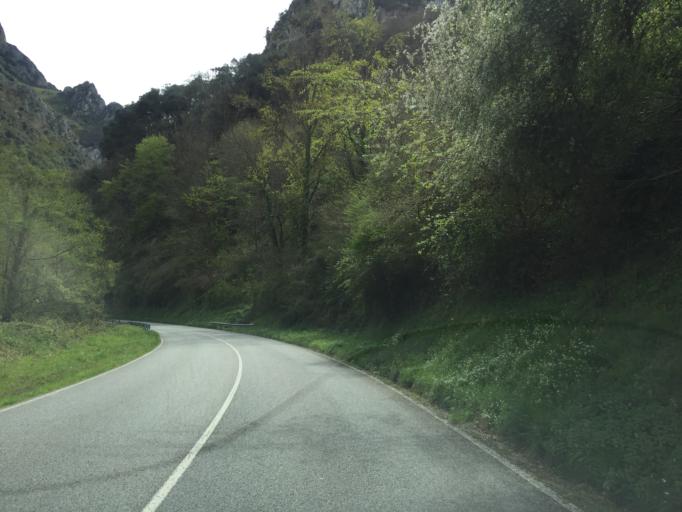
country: ES
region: Asturias
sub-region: Province of Asturias
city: Proaza
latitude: 43.2400
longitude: -6.0308
